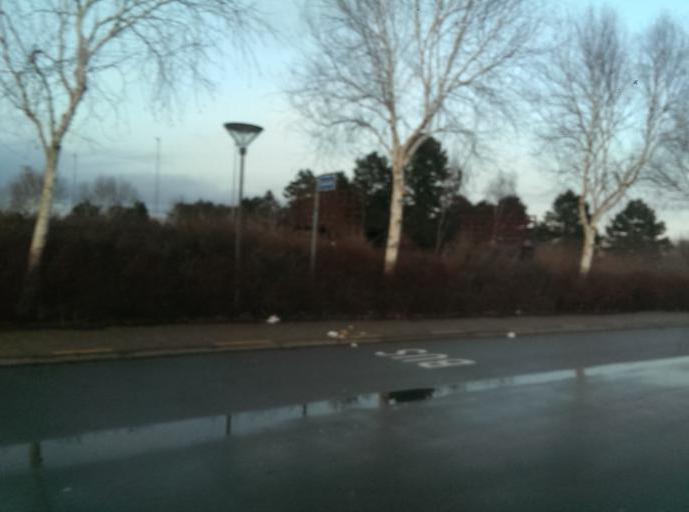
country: DK
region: South Denmark
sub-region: Varde Kommune
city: Varde
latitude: 55.6328
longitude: 8.4732
